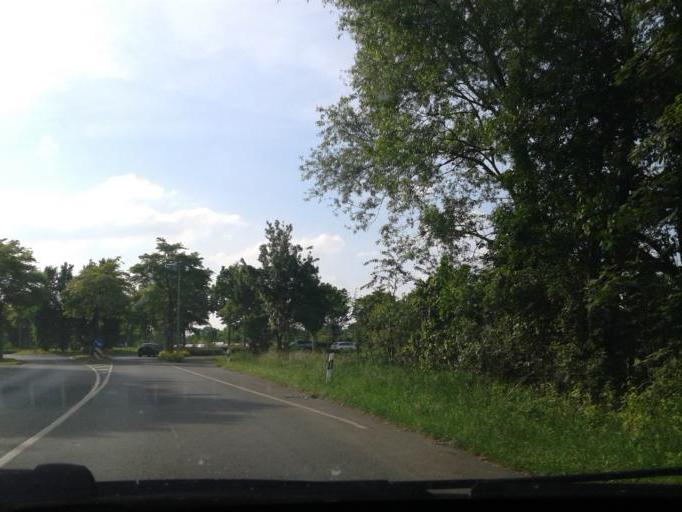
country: DE
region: North Rhine-Westphalia
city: Bad Lippspringe
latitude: 51.7708
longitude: 8.8001
